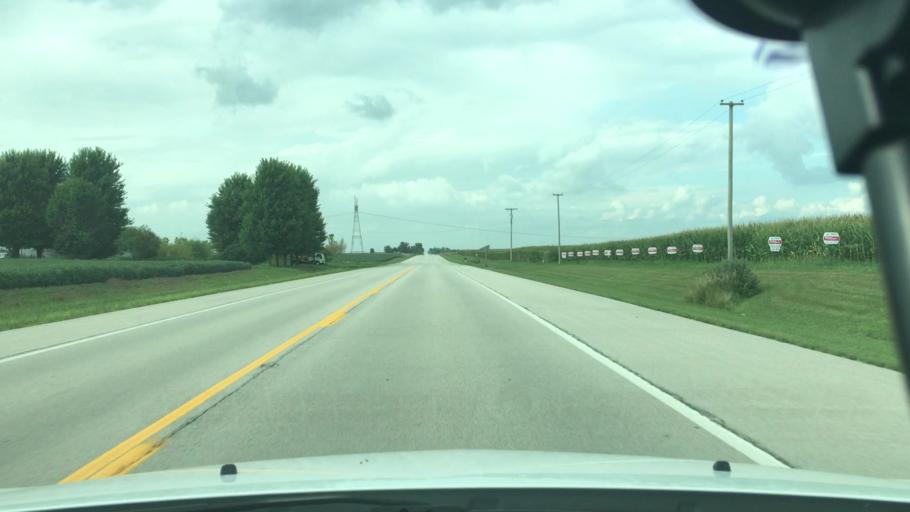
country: US
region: Illinois
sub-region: DeKalb County
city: Waterman
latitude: 41.7968
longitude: -88.7540
